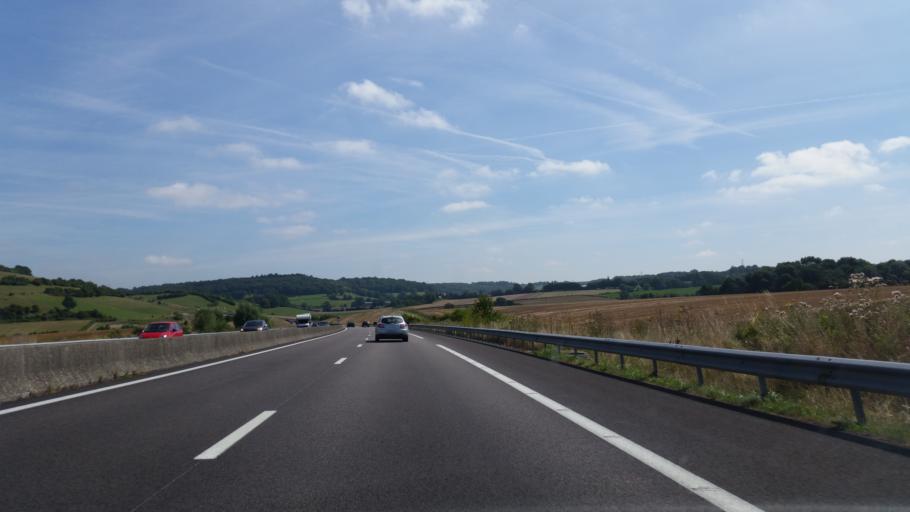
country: FR
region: Haute-Normandie
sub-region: Departement de la Seine-Maritime
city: Gaillefontaine
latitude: 49.7349
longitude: 1.5582
